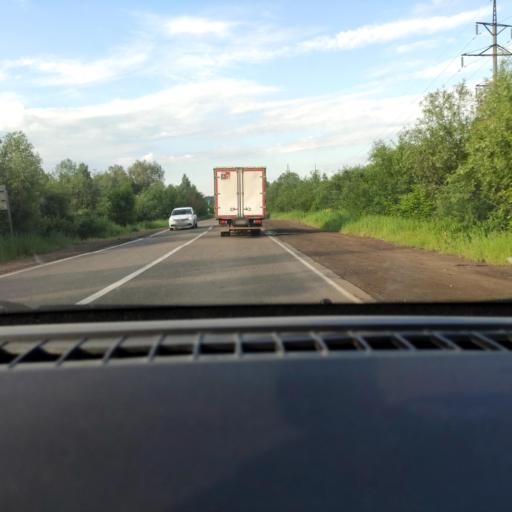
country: RU
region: Udmurtiya
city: Votkinsk
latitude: 57.0479
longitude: 54.0382
